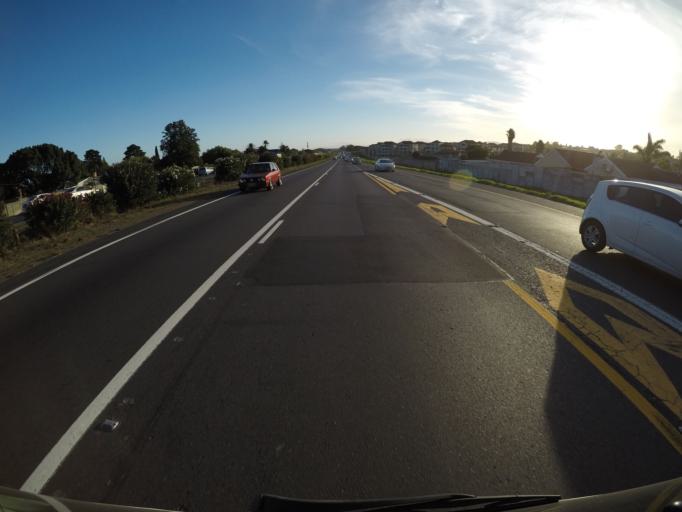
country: ZA
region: Western Cape
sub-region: City of Cape Town
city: Kraaifontein
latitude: -33.8611
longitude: 18.6905
